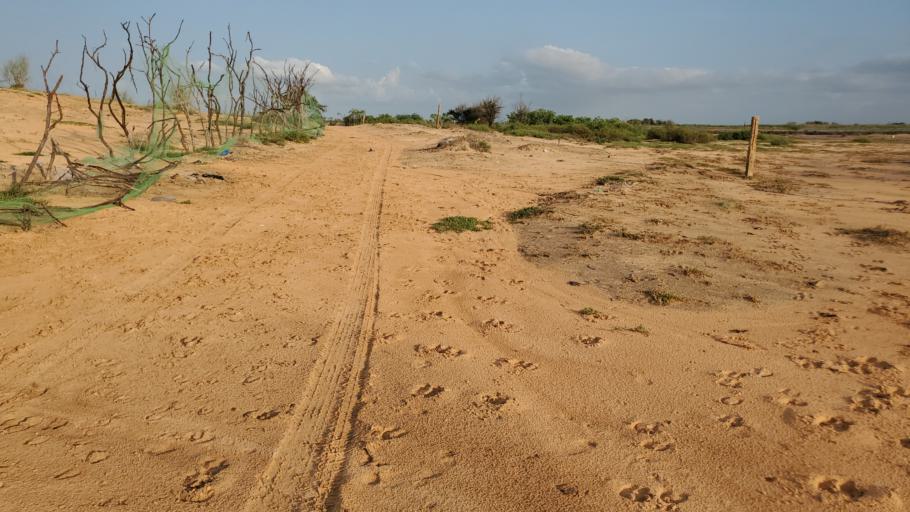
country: SN
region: Saint-Louis
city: Saint-Louis
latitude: 16.0470
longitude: -16.4165
